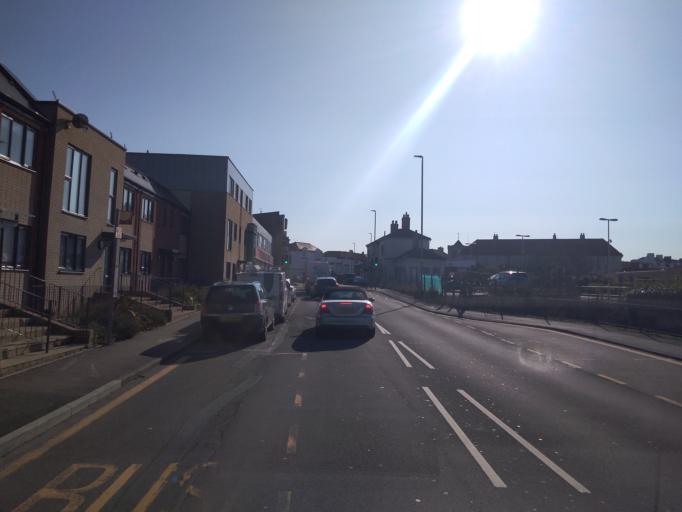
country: GB
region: England
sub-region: East Sussex
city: Seaford
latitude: 50.7736
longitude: 0.0990
